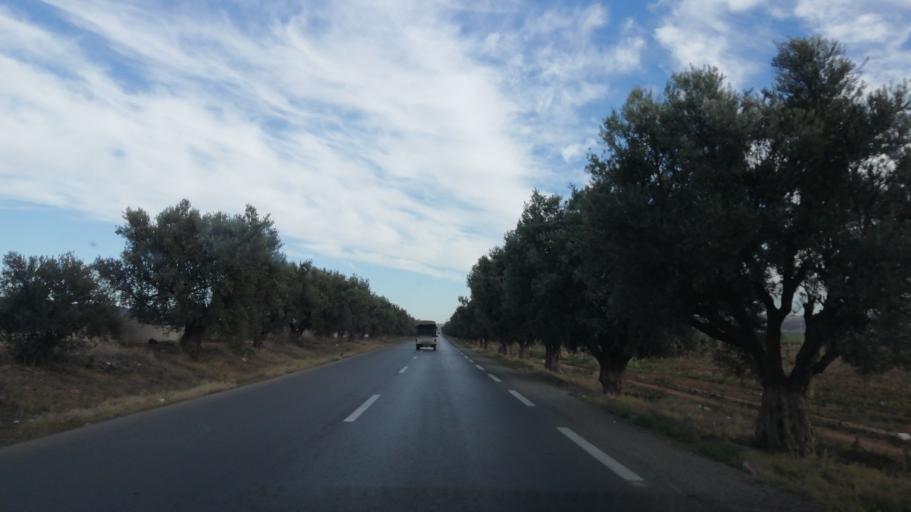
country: DZ
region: Sidi Bel Abbes
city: Sidi Bel Abbes
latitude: 35.1782
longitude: -0.4363
